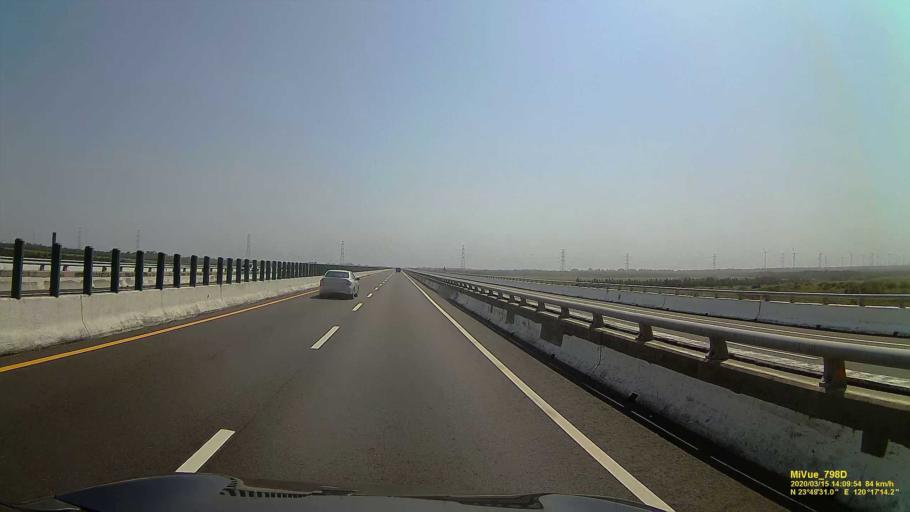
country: TW
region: Taiwan
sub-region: Yunlin
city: Douliu
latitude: 23.8251
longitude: 120.2877
